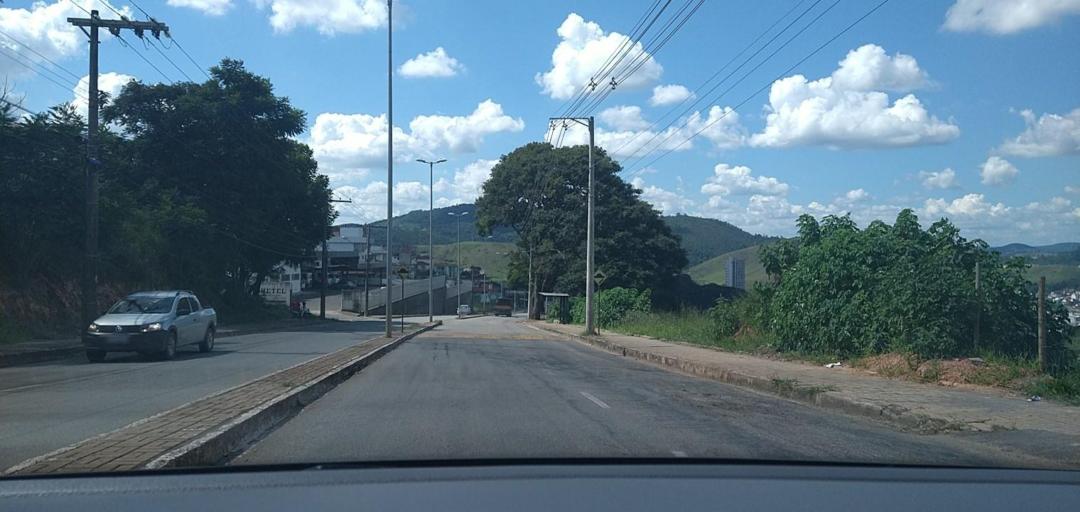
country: BR
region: Minas Gerais
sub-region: Joao Monlevade
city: Joao Monlevade
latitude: -19.8247
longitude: -43.1895
